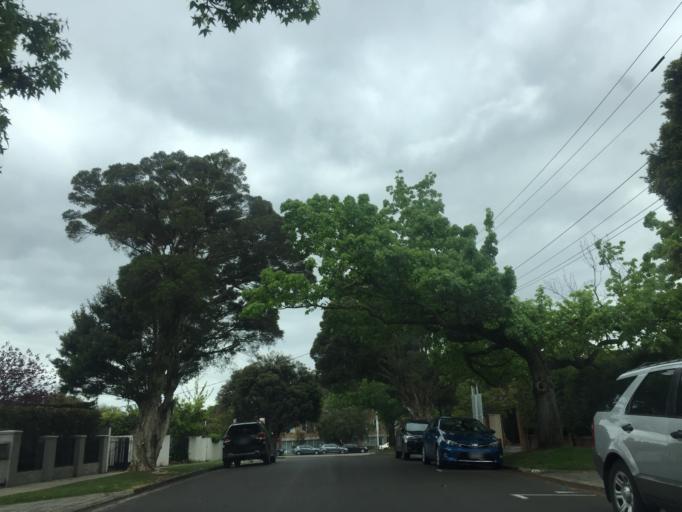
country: AU
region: Victoria
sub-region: Boroondara
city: Kew East
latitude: -37.8102
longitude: 145.0523
